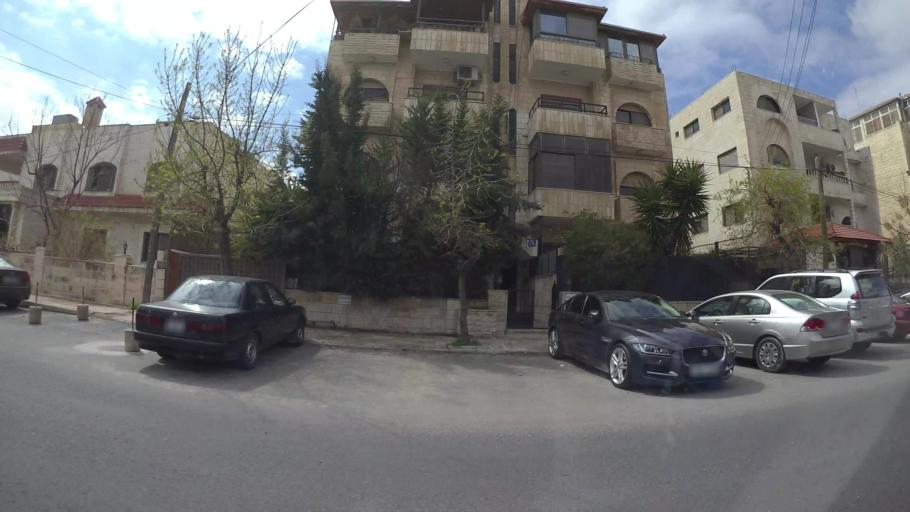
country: JO
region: Amman
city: Wadi as Sir
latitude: 31.9688
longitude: 35.8407
